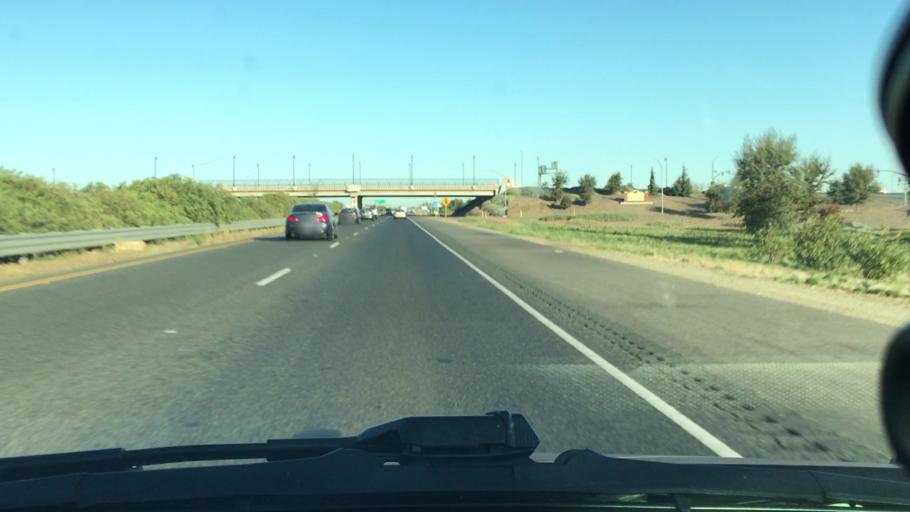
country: US
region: California
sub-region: Sacramento County
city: Elk Grove
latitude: 38.3746
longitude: -121.3600
